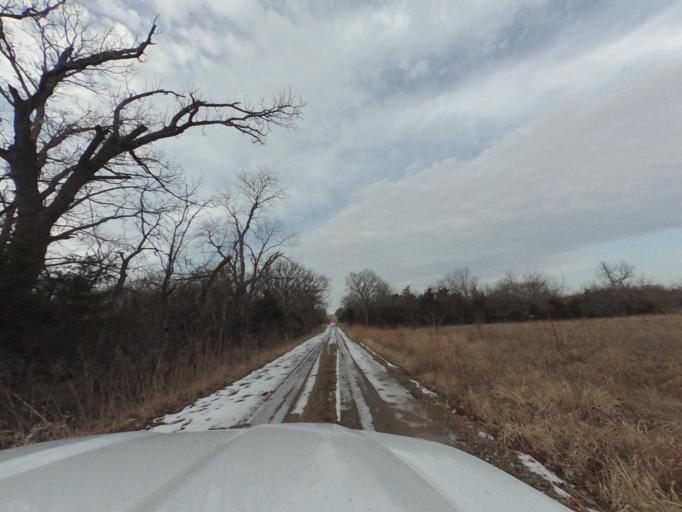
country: US
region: Kansas
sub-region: Chase County
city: Cottonwood Falls
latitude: 38.4784
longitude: -96.4385
